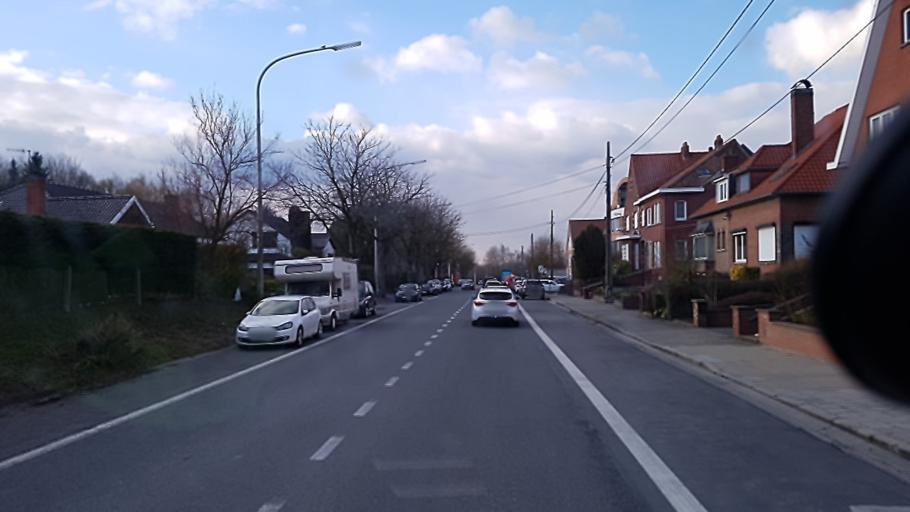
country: BE
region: Wallonia
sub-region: Province du Hainaut
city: Estaimpuis
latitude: 50.7258
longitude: 3.2986
